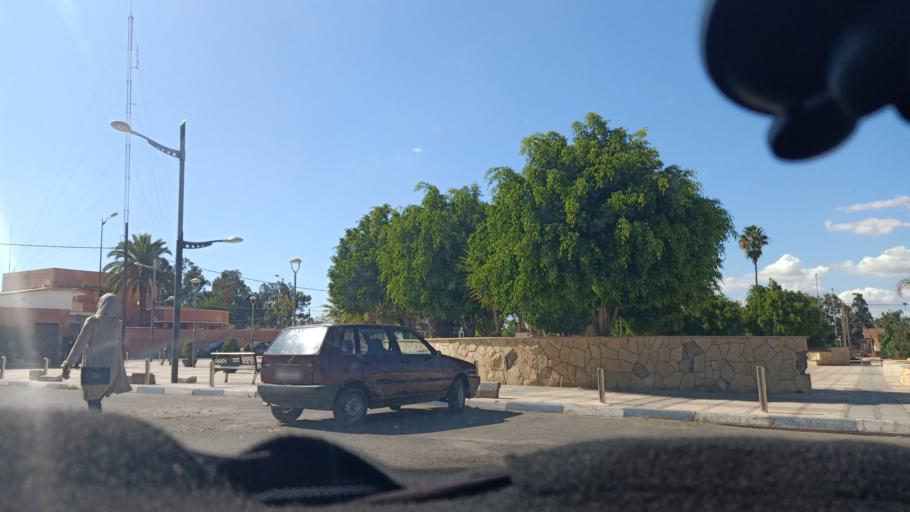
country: MA
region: Doukkala-Abda
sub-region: Safi
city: Youssoufia
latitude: 32.2466
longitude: -8.5333
